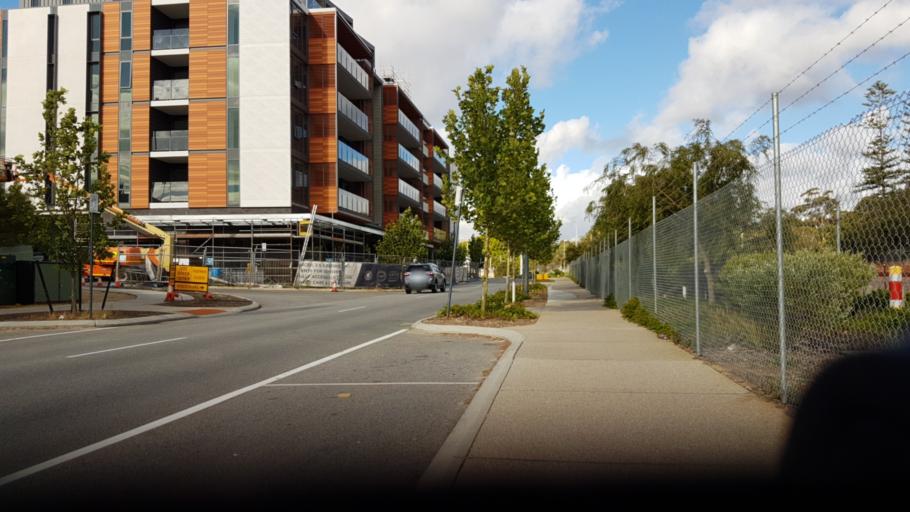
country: AU
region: Western Australia
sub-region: Claremont
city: Claremont
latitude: -31.9794
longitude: 115.7837
